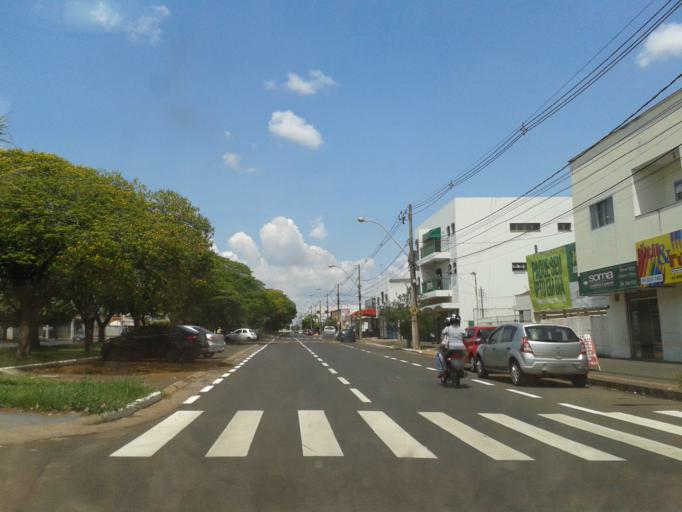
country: BR
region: Minas Gerais
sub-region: Araguari
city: Araguari
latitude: -18.6579
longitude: -48.1912
